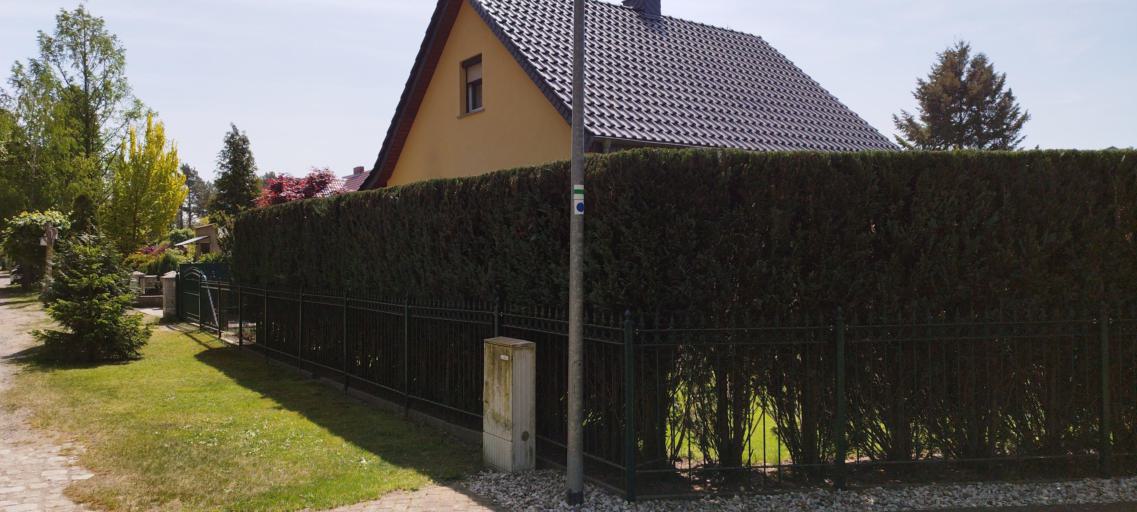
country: DE
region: Brandenburg
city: Spreenhagen
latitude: 52.3960
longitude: 13.9378
